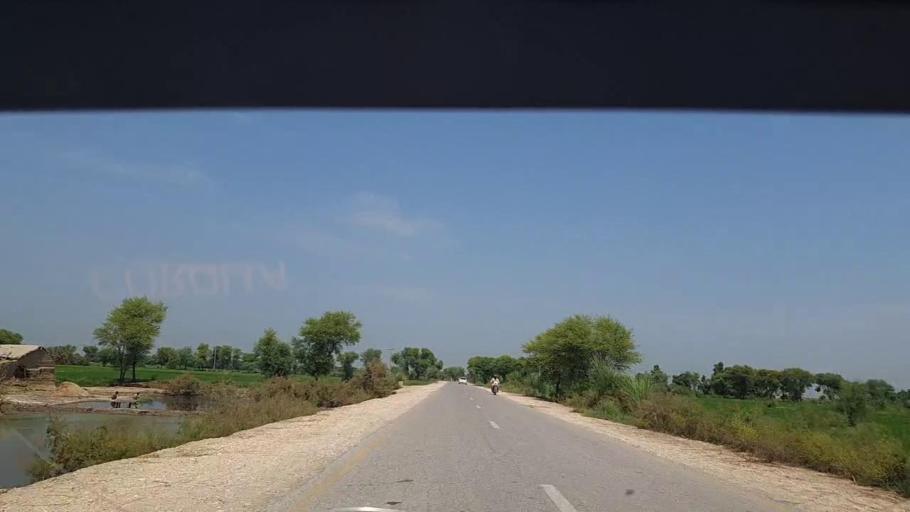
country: PK
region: Sindh
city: Thul
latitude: 28.1405
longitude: 68.8176
